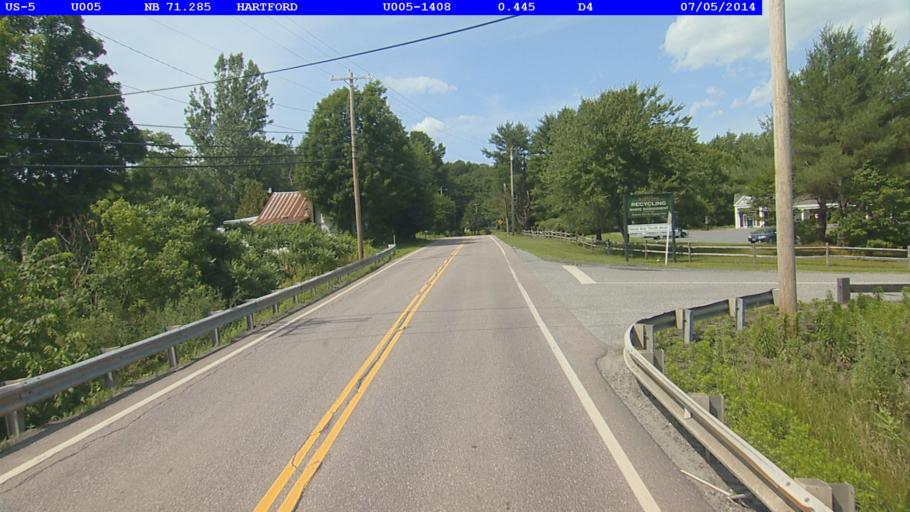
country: US
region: Vermont
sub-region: Windsor County
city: White River Junction
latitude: 43.6171
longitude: -72.3553
